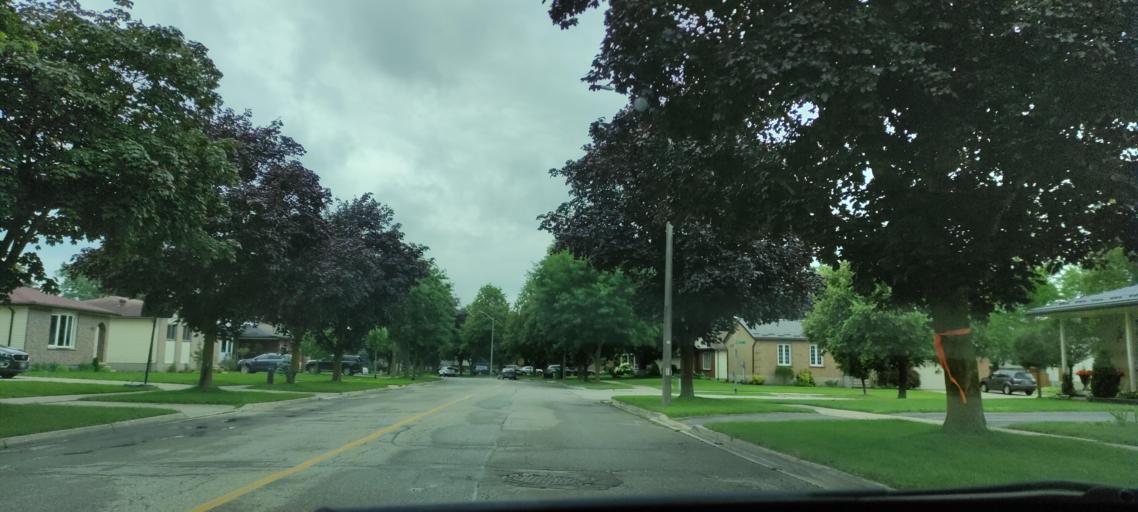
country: CA
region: Ontario
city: Stratford
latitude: 43.3825
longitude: -80.9795
